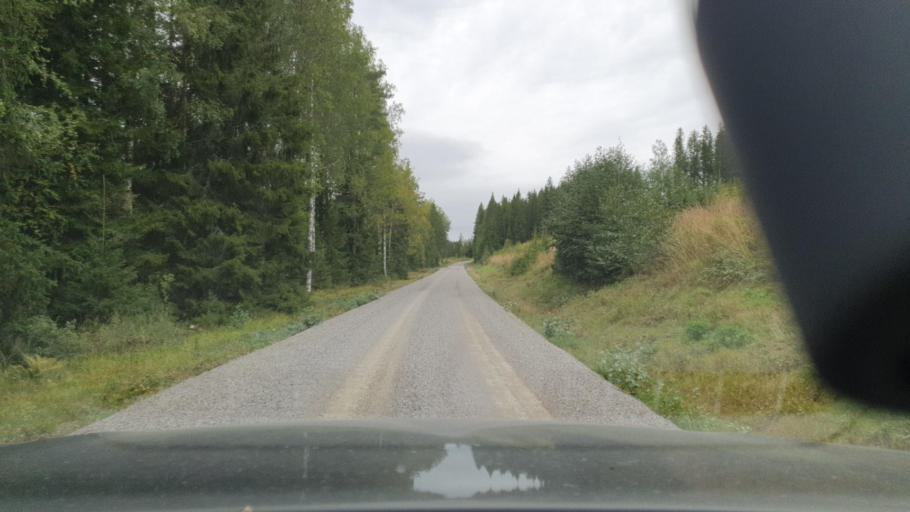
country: SE
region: Vaermland
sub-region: Eda Kommun
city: Charlottenberg
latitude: 60.0557
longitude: 12.6268
